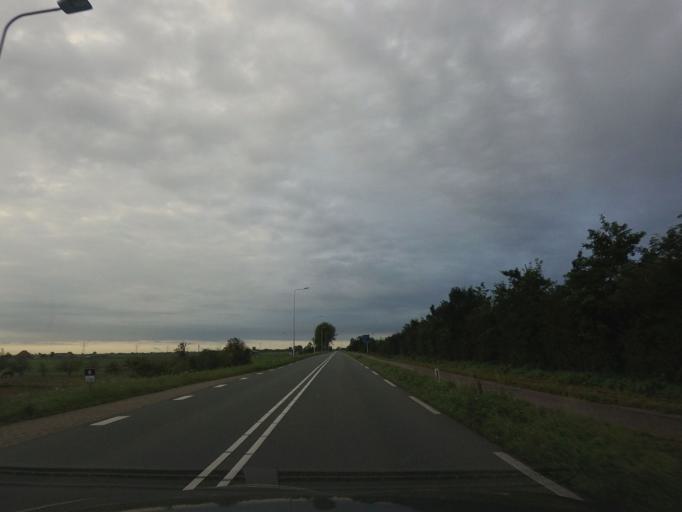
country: NL
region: North Holland
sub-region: Gemeente Uitgeest
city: Uitgeest
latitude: 52.5496
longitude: 4.7795
